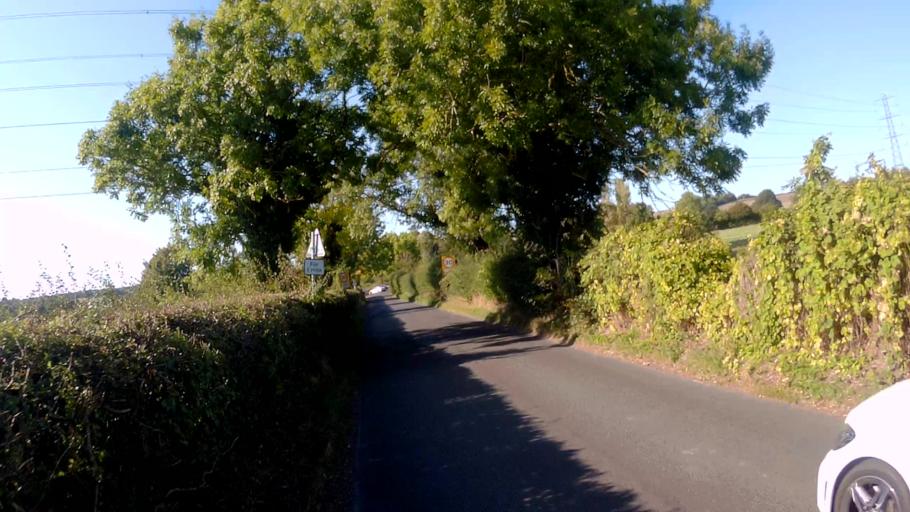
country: GB
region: England
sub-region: Hampshire
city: Long Sutton
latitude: 51.1875
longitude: -0.9024
